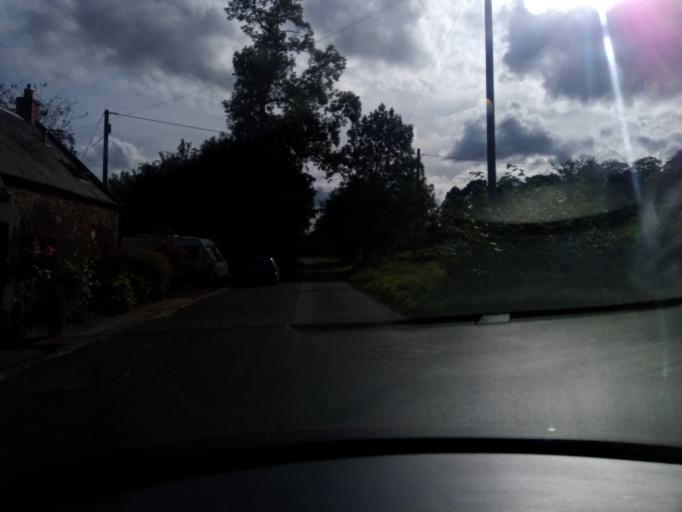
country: GB
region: Scotland
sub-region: The Scottish Borders
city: Kelso
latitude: 55.4978
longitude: -2.3474
